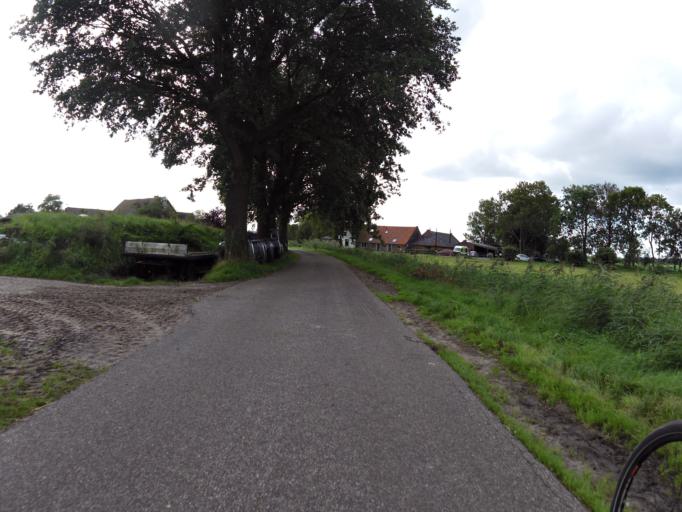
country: NL
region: North Holland
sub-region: Gemeente Wijdemeren
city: Nieuw-Loosdrecht
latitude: 52.1800
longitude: 5.1447
